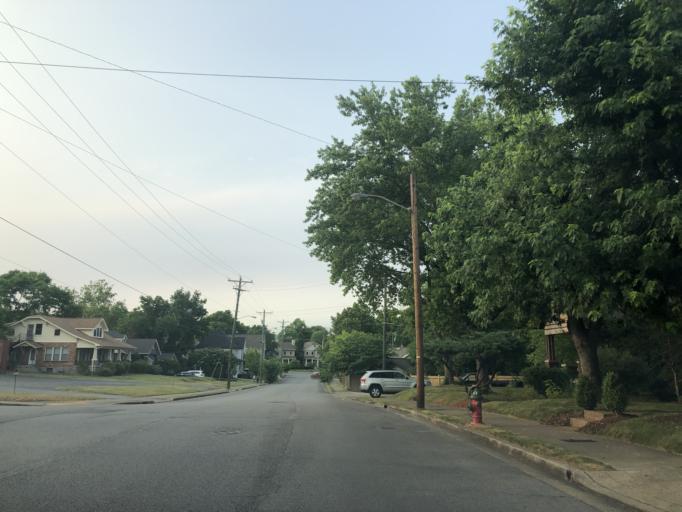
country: US
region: Tennessee
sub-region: Davidson County
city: Nashville
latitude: 36.1284
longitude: -86.7830
